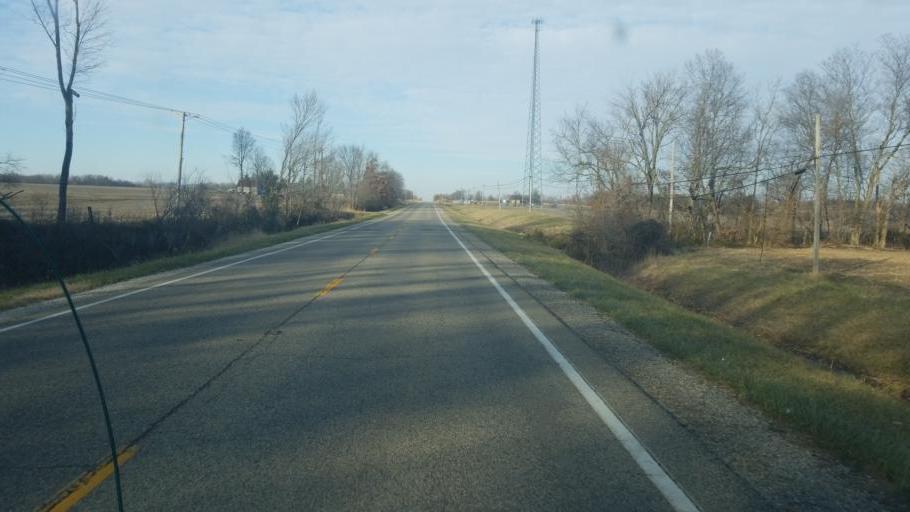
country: US
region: Illinois
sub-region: Lawrence County
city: Lawrenceville
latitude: 38.6664
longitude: -87.6942
